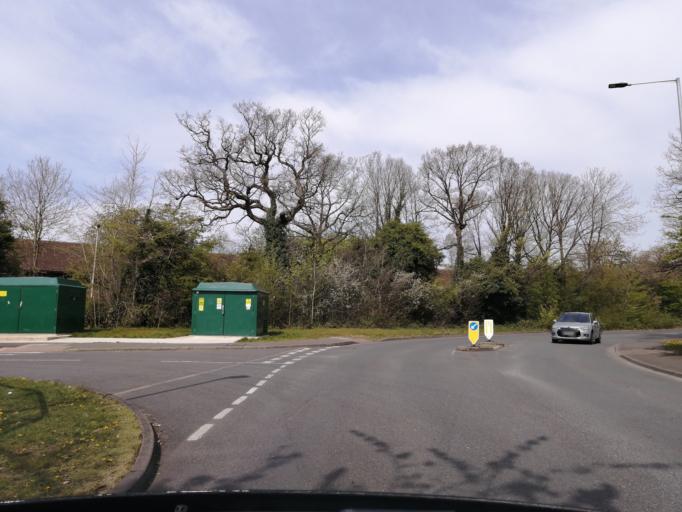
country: GB
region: England
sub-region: Peterborough
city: Marholm
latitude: 52.5891
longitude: -0.2849
